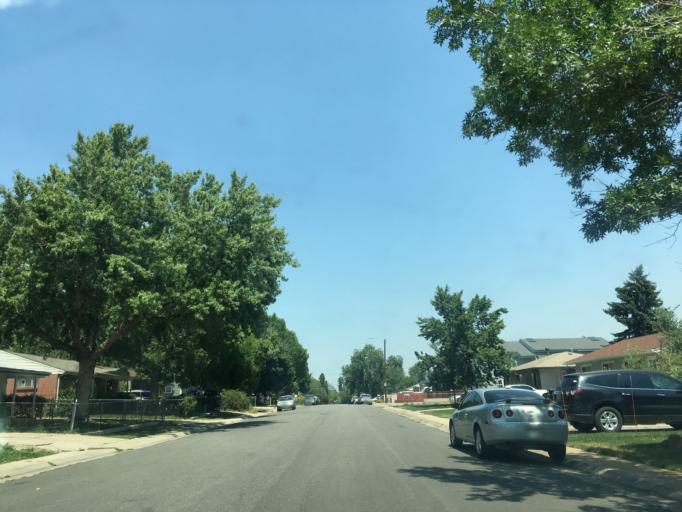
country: US
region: Colorado
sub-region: Arapahoe County
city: Sheridan
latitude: 39.6950
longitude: -105.0310
